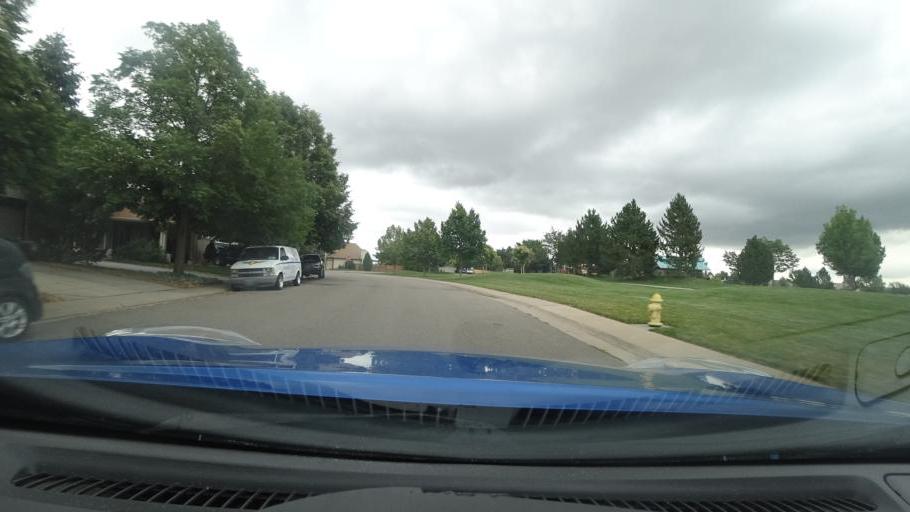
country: US
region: Colorado
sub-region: Adams County
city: Aurora
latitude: 39.7018
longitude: -104.8165
